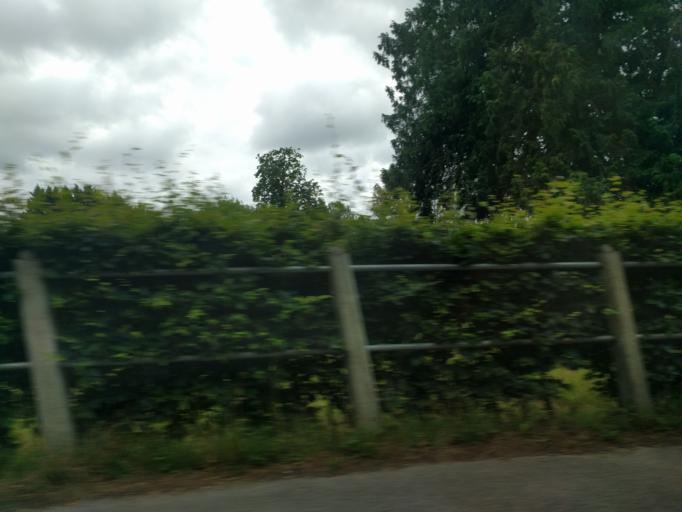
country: GB
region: England
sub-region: Hampshire
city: Totton
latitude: 50.8905
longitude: -1.5277
